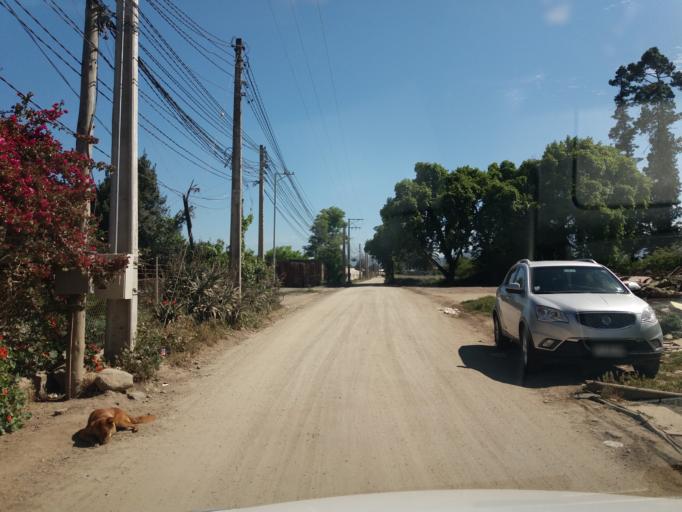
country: CL
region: Valparaiso
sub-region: Provincia de Quillota
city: Quillota
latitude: -32.8767
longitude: -71.2252
